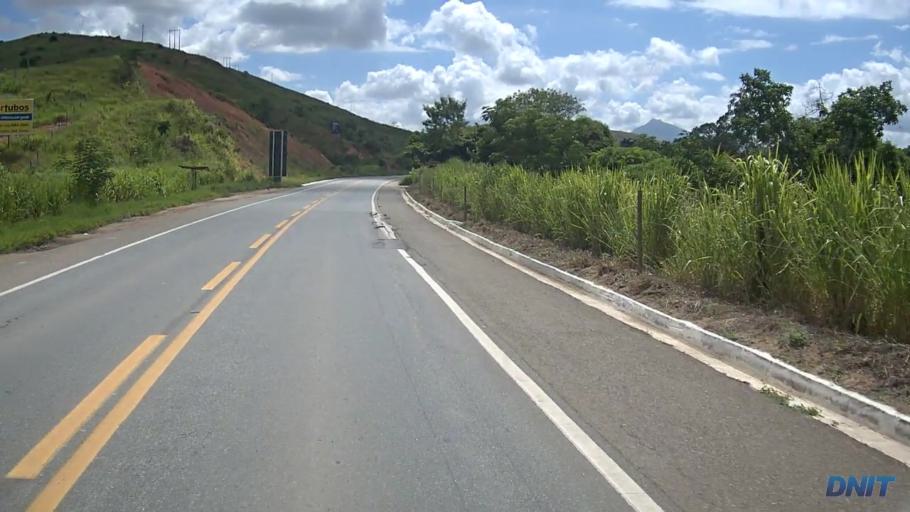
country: BR
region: Minas Gerais
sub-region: Governador Valadares
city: Governador Valadares
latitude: -18.9301
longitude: -42.0449
